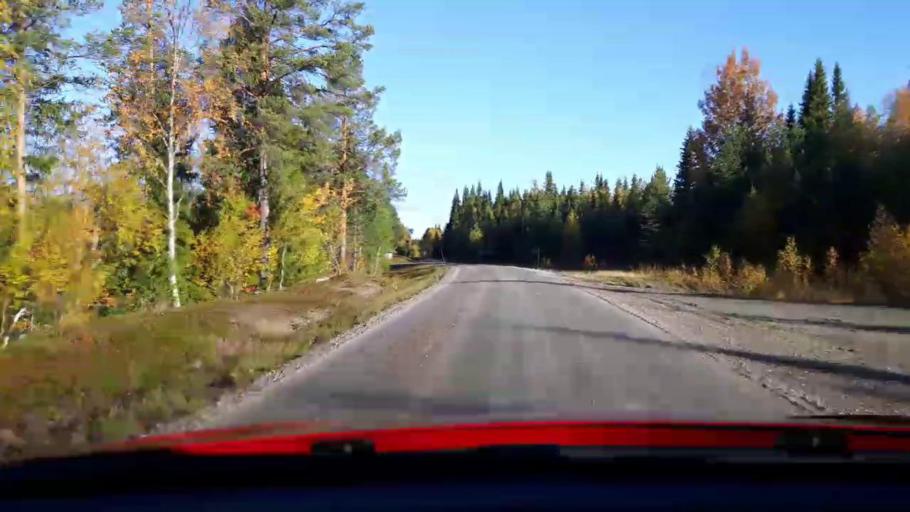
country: SE
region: Jaemtland
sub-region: Stroemsunds Kommun
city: Stroemsund
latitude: 64.3939
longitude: 15.1489
